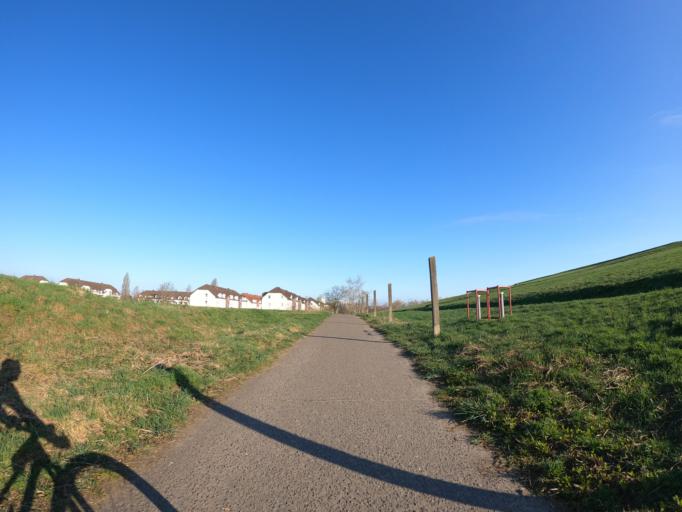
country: DE
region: Berlin
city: Gropiusstadt
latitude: 52.4089
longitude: 13.4513
